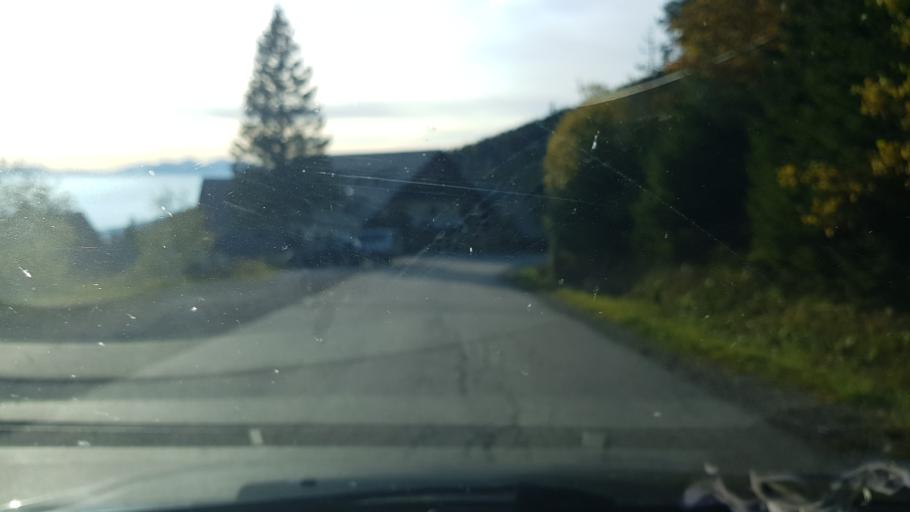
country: SI
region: Mislinja
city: Mislinja
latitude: 46.5019
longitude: 15.2092
